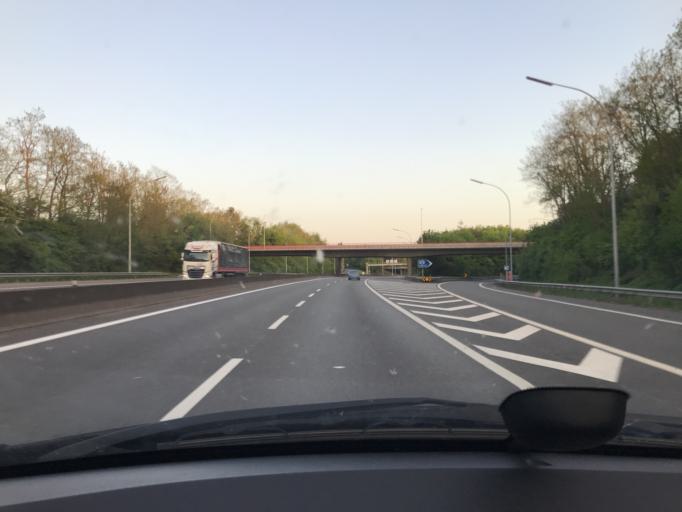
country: LU
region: Luxembourg
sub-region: Canton de Luxembourg
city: Strassen
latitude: 49.6241
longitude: 6.0811
